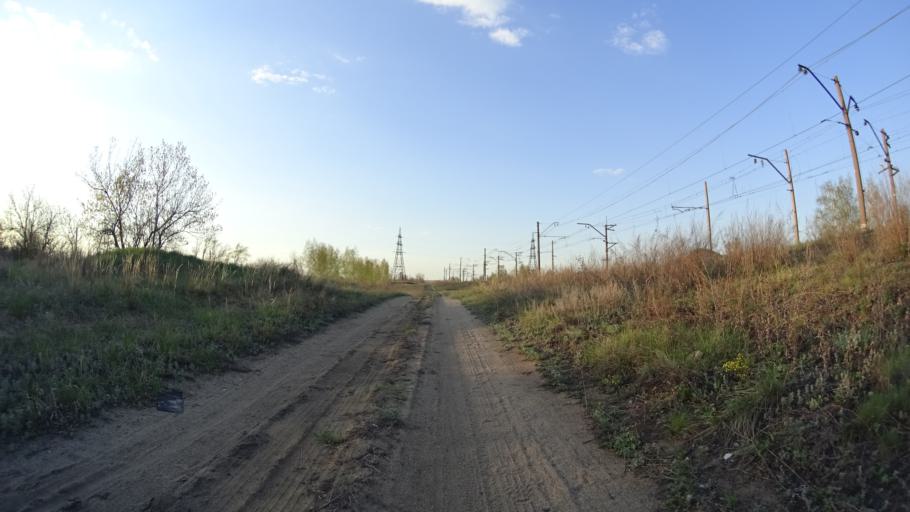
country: RU
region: Chelyabinsk
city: Troitsk
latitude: 54.0592
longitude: 61.6135
